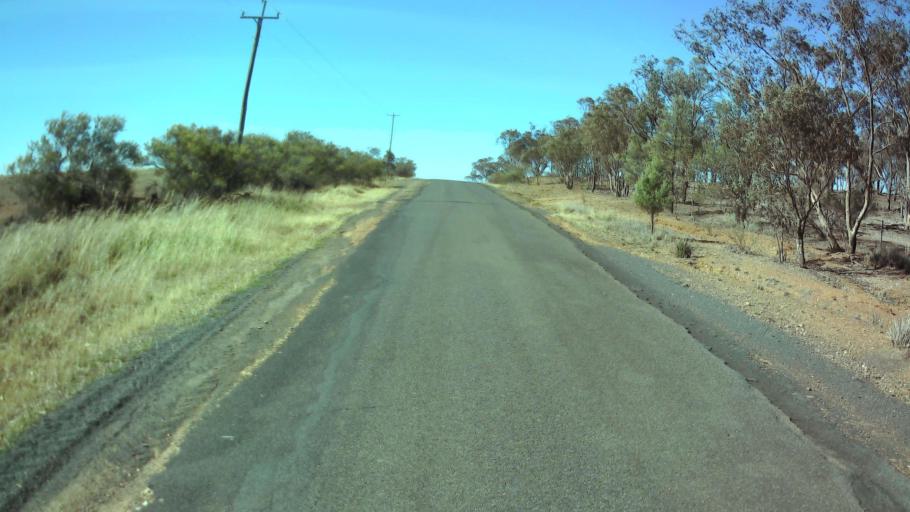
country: AU
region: New South Wales
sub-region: Weddin
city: Grenfell
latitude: -33.7642
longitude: 147.8289
